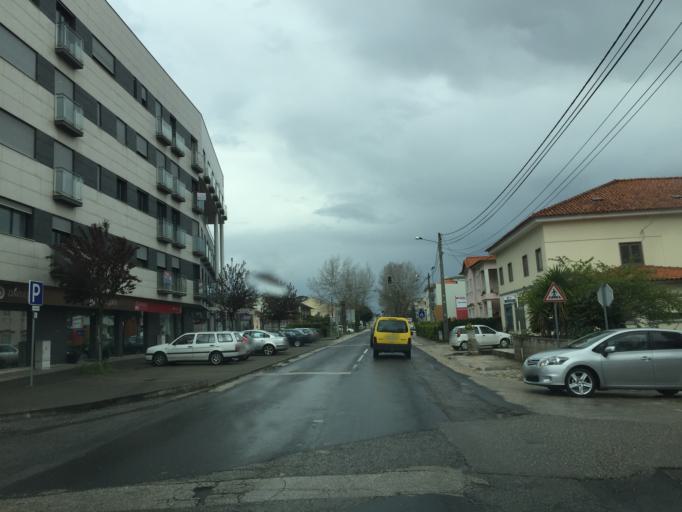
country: PT
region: Santarem
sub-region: Ourem
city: Fatima
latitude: 39.6354
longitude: -8.6840
